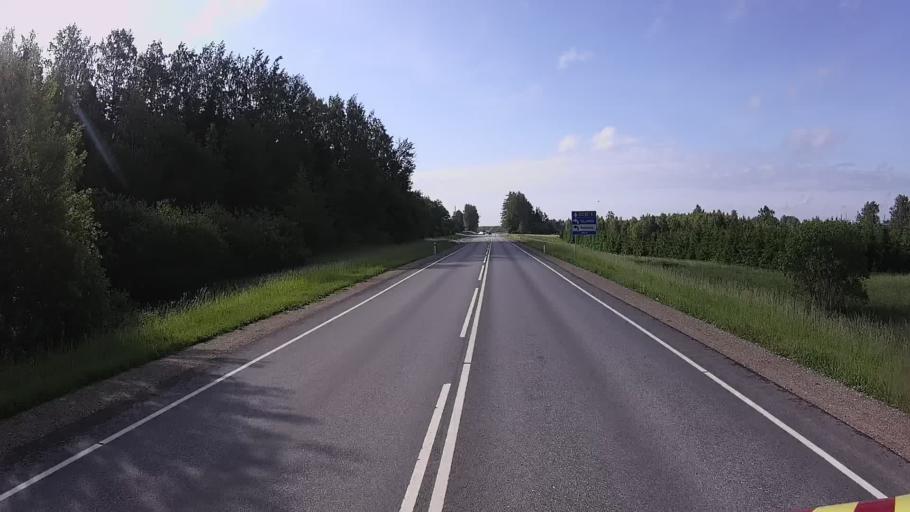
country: EE
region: Viljandimaa
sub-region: Viljandi linn
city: Viljandi
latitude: 58.3483
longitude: 25.5633
